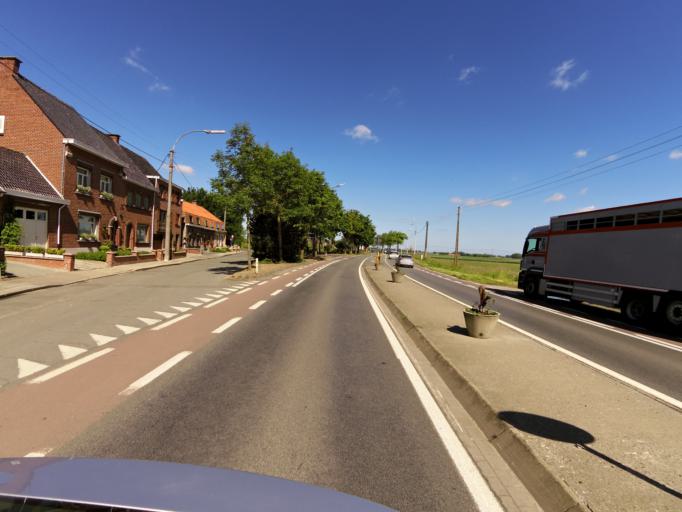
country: BE
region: Flanders
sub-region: Provincie West-Vlaanderen
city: Ieper
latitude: 50.8695
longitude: 2.8452
